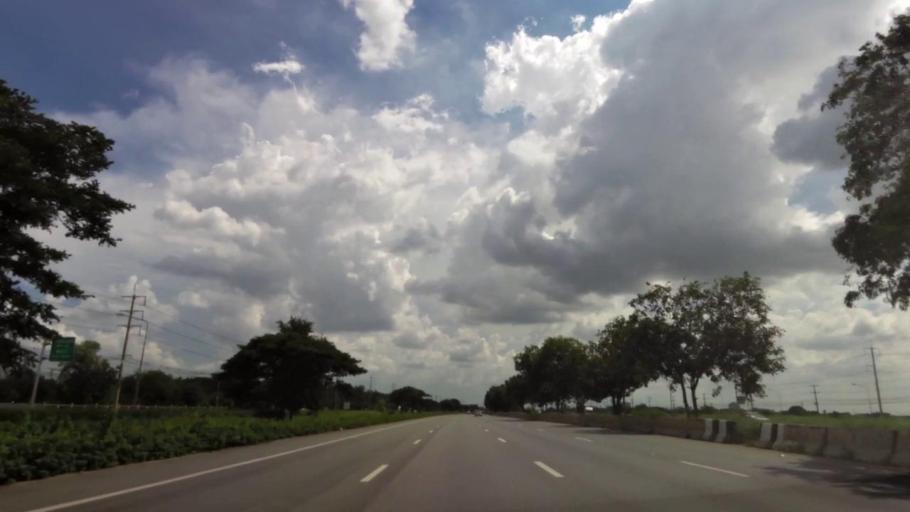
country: TH
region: Phra Nakhon Si Ayutthaya
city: Phra Nakhon Si Ayutthaya
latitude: 14.3669
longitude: 100.6117
